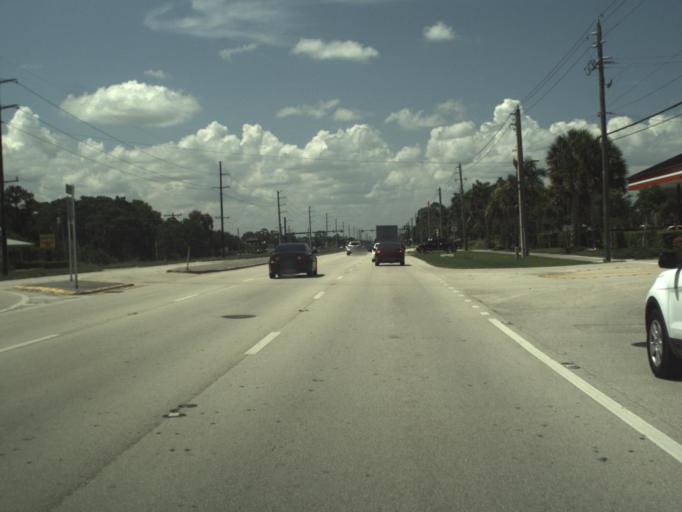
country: US
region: Florida
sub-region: Martin County
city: North River Shores
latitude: 27.2259
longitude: -80.2648
